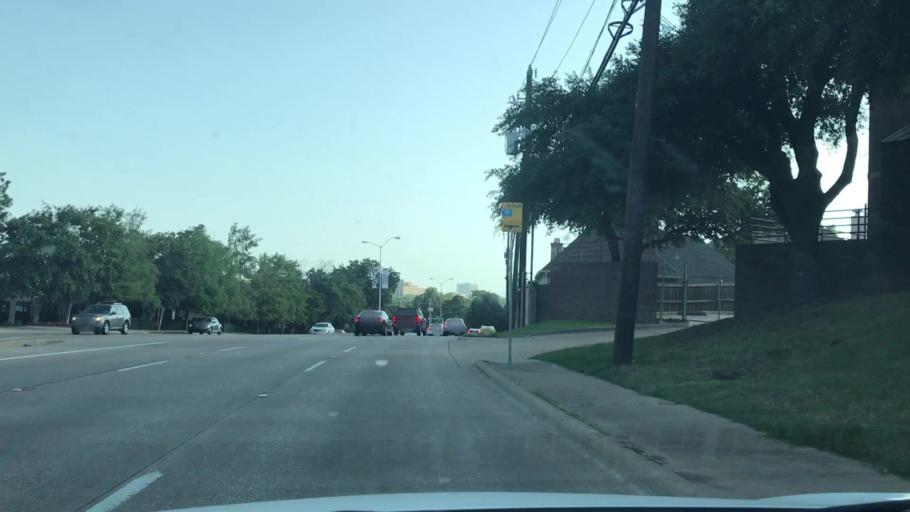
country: US
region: Texas
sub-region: Dallas County
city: Richardson
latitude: 32.8956
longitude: -96.7519
